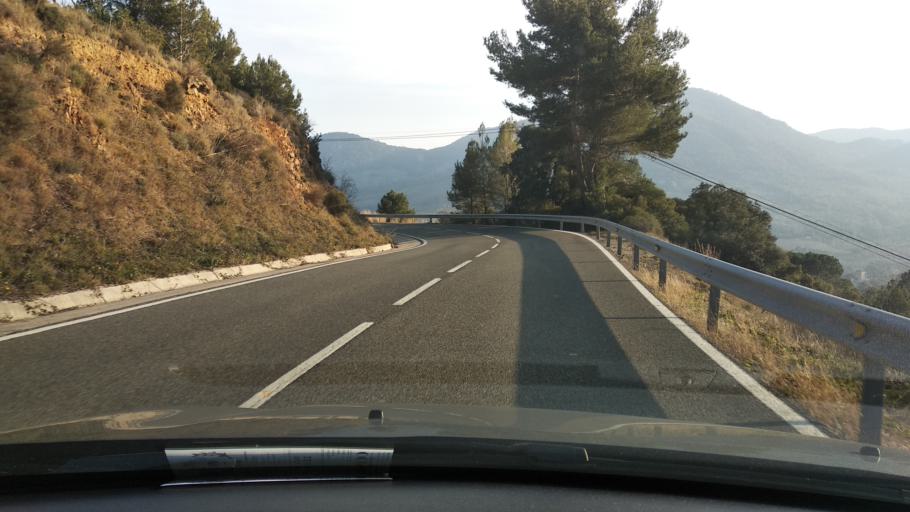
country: ES
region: Catalonia
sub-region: Provincia de Tarragona
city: Alforja
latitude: 41.2192
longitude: 0.9507
